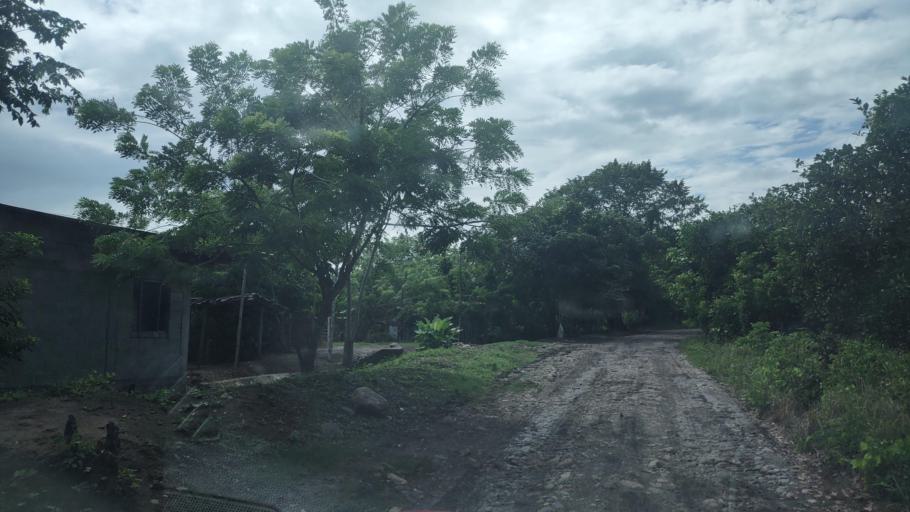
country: MX
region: Veracruz
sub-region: Atzalan
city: Colonias Pedernales
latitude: 20.0586
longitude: -97.0105
